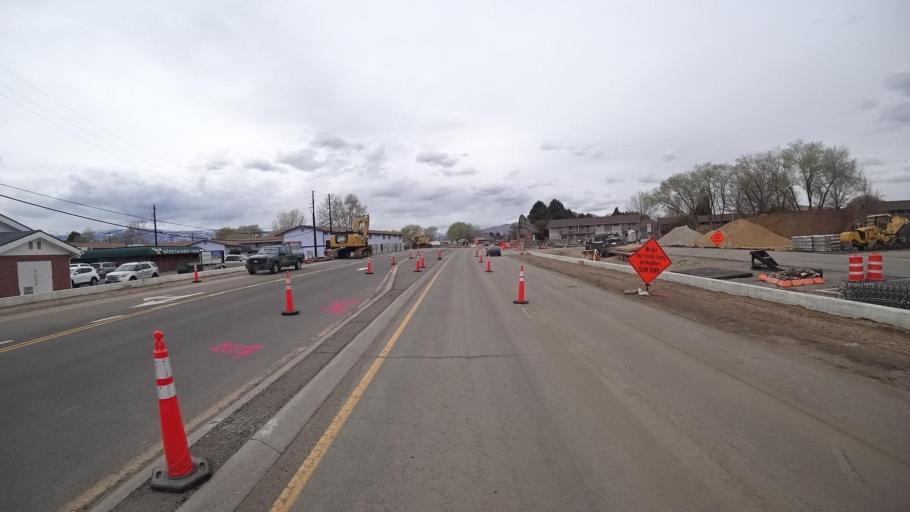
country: US
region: Nevada
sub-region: Washoe County
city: Sparks
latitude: 39.5439
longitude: -119.7539
